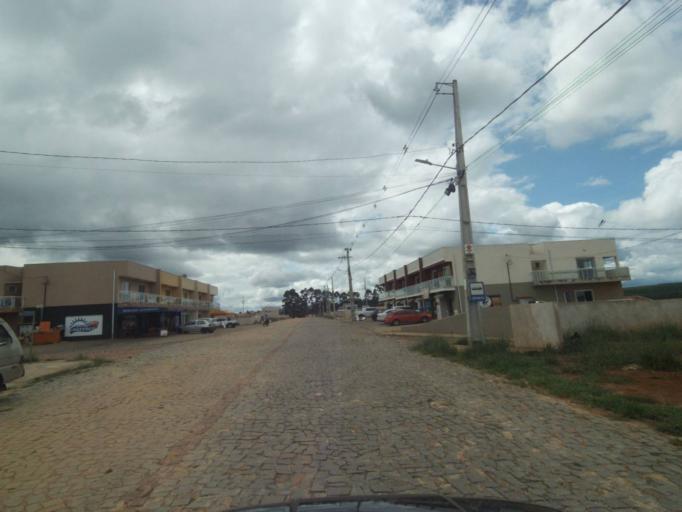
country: BR
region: Parana
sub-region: Telemaco Borba
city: Telemaco Borba
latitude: -24.3082
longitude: -50.6354
